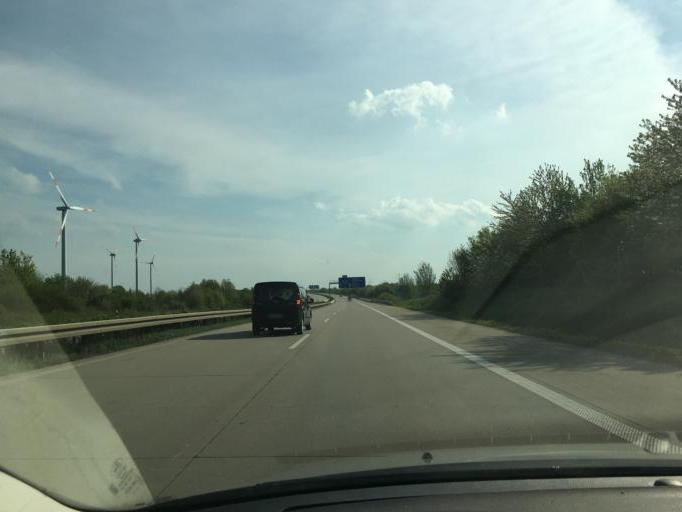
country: DE
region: Saxony-Anhalt
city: Dahlenwarsleben
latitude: 52.1843
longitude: 11.5492
